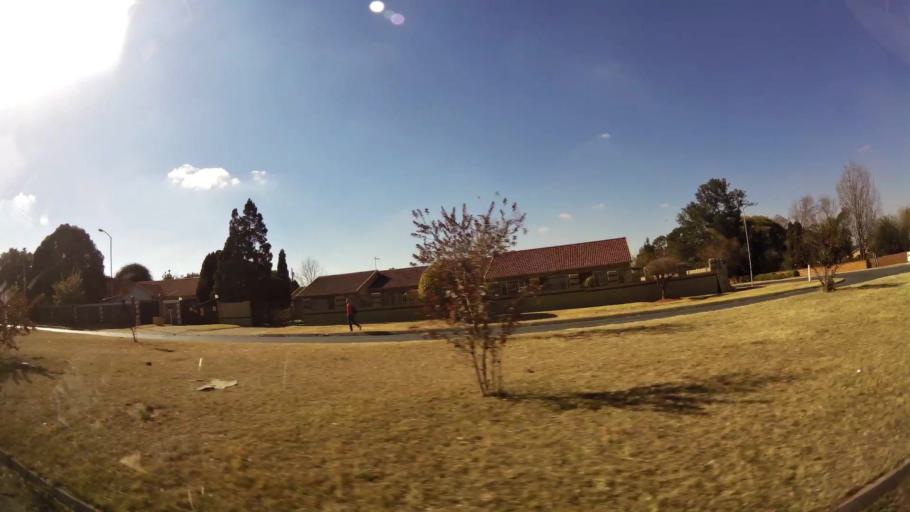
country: ZA
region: Gauteng
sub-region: City of Johannesburg Metropolitan Municipality
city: Roodepoort
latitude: -26.1443
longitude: 27.8347
